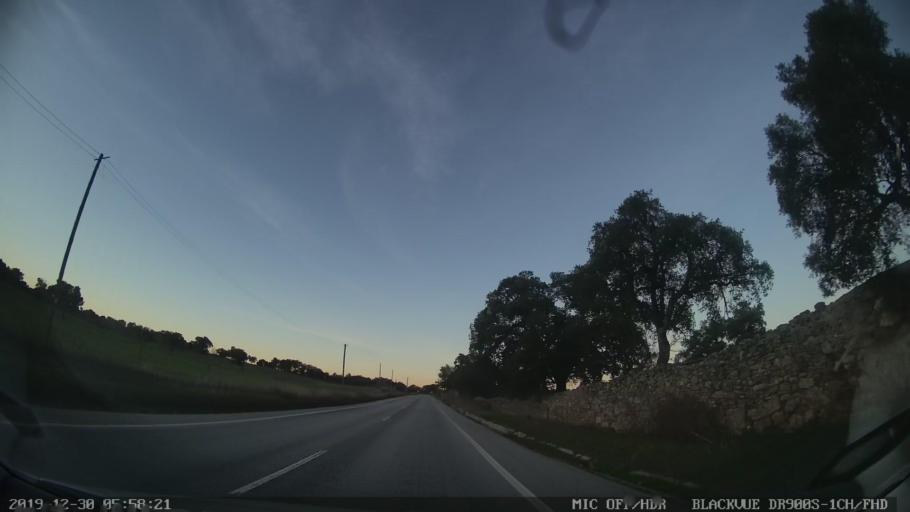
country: PT
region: Castelo Branco
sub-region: Idanha-A-Nova
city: Idanha-a-Nova
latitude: 40.0339
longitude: -7.2416
